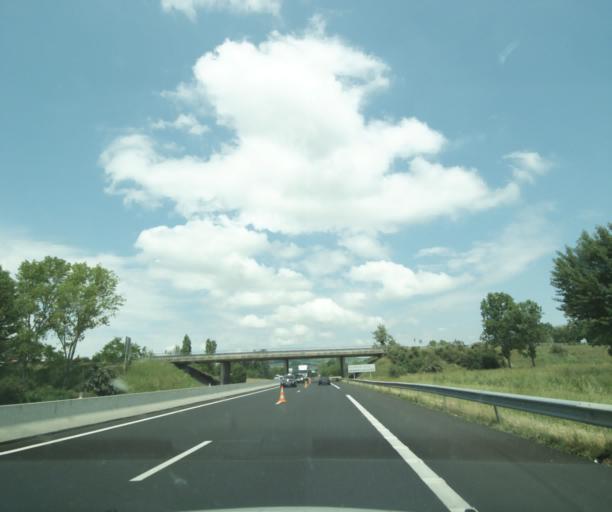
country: FR
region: Auvergne
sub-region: Departement du Puy-de-Dome
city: Issoire
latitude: 45.5418
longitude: 3.2669
